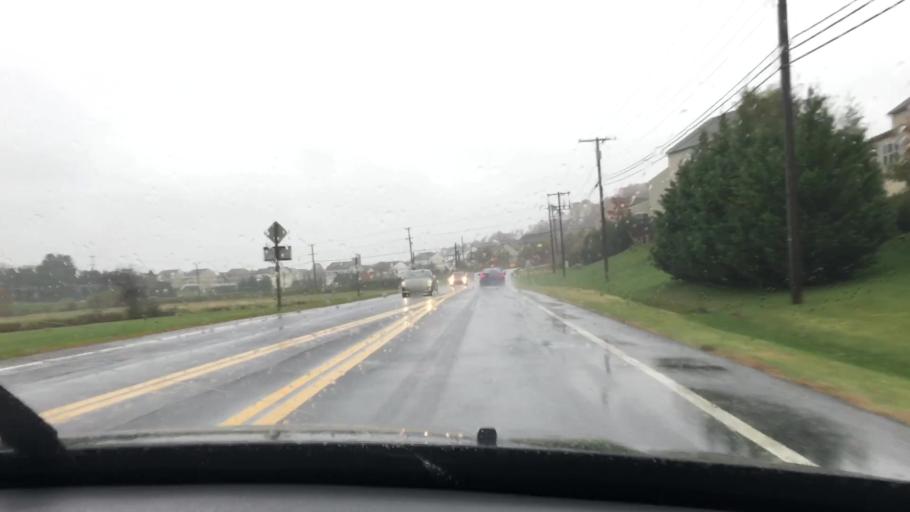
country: US
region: Maryland
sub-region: Carroll County
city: Manchester
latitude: 39.6812
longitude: -76.8896
